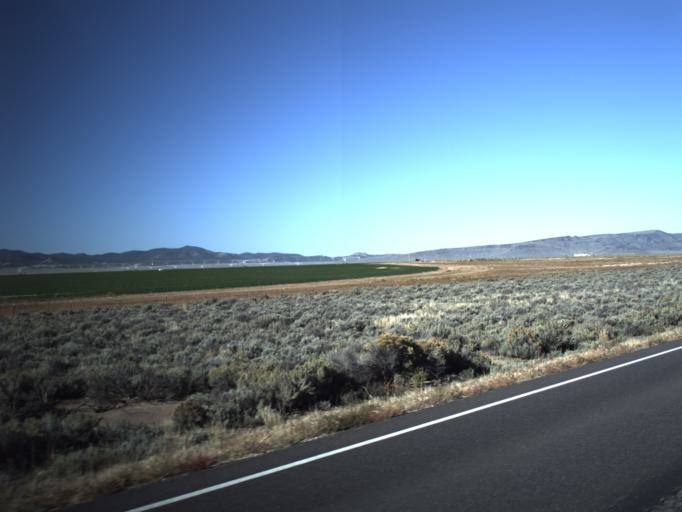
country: US
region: Utah
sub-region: Washington County
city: Enterprise
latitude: 37.7525
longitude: -113.7769
